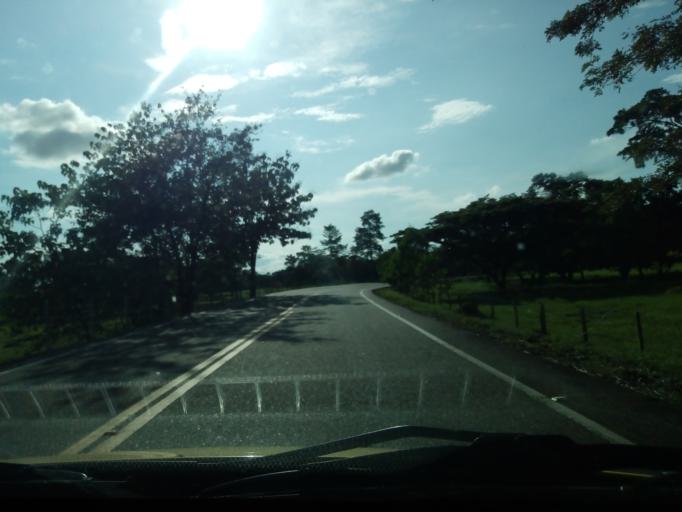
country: CO
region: Boyaca
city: Puerto Boyaca
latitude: 5.9323
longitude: -74.5348
